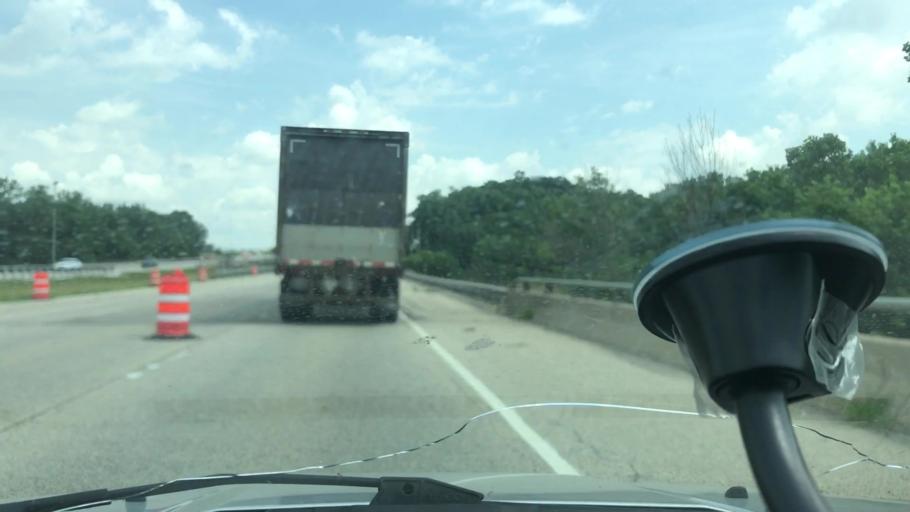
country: US
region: Illinois
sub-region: Peoria County
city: Bellevue
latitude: 40.7317
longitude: -89.6725
